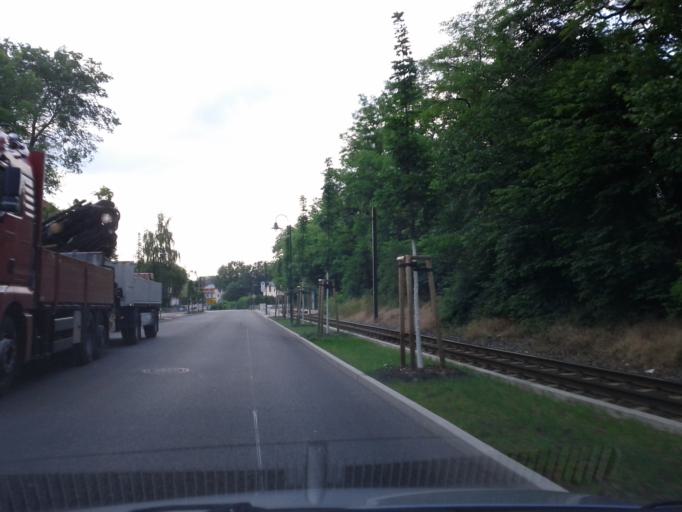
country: DE
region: Brandenburg
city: Woltersdorf
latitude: 52.4725
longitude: 13.7774
